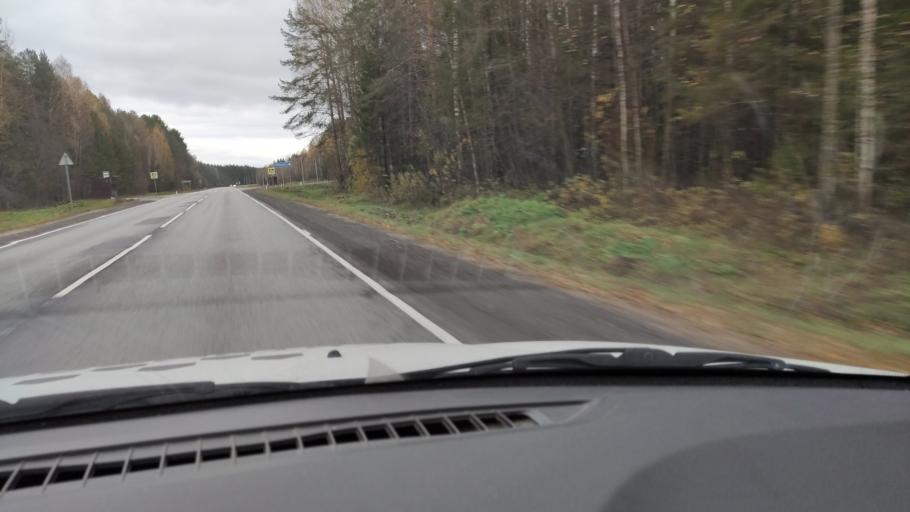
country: RU
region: Kirov
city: Belaya Kholunitsa
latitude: 58.8296
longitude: 50.6549
